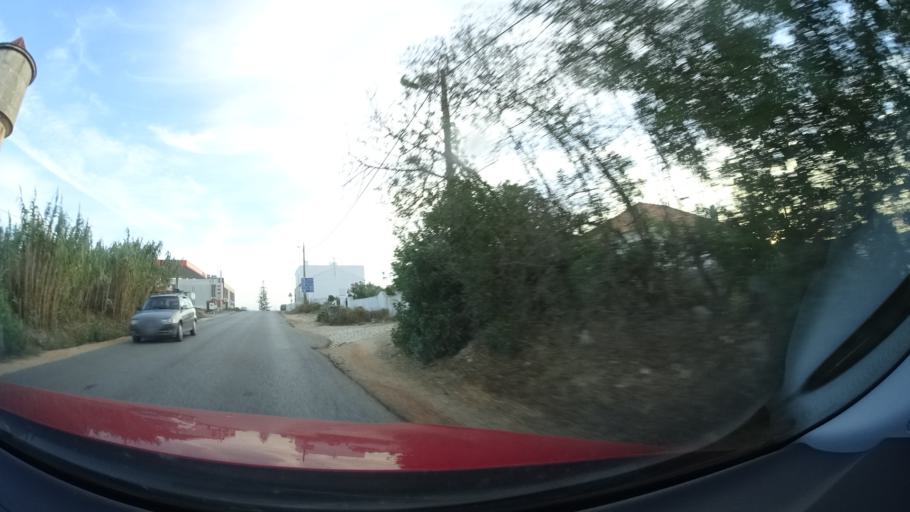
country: PT
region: Faro
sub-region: Vila do Bispo
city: Sagres
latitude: 37.0093
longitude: -8.9442
